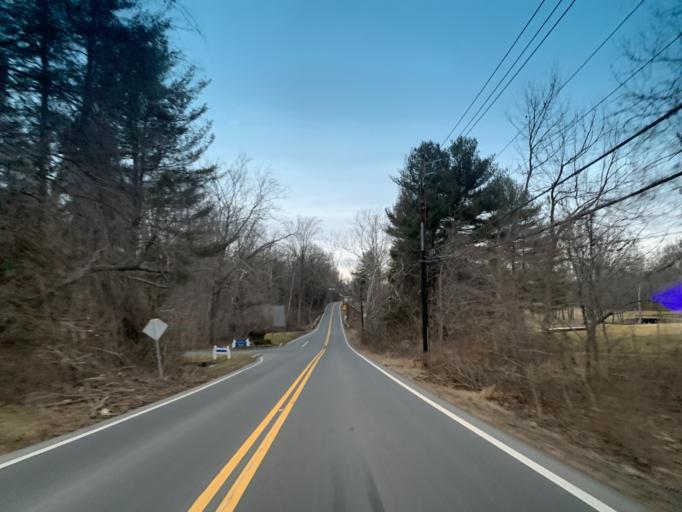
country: US
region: Maryland
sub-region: Montgomery County
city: Layhill
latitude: 39.1140
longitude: -77.0370
